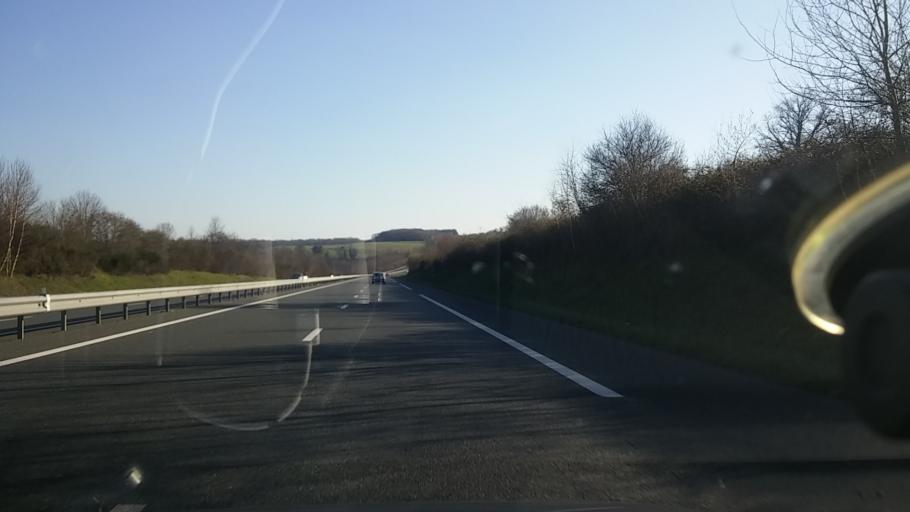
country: FR
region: Limousin
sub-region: Departement de la Haute-Vienne
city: Saint-Sulpice-les-Feuilles
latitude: 46.3857
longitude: 1.4489
